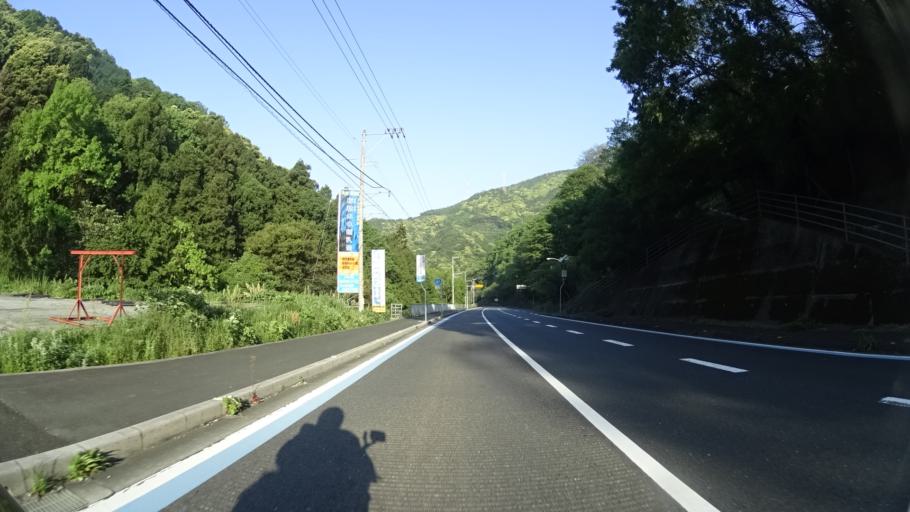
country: JP
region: Ehime
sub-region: Nishiuwa-gun
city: Ikata-cho
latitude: 33.4974
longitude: 132.3755
